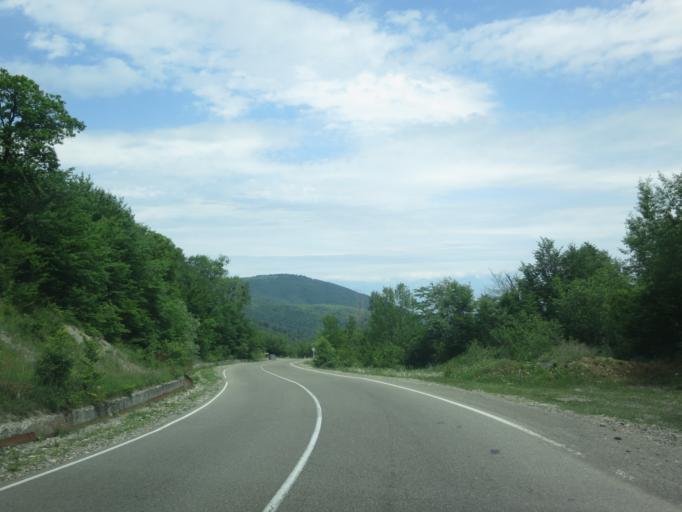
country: GE
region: Kakheti
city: Sagarejo
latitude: 41.8653
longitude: 45.3470
